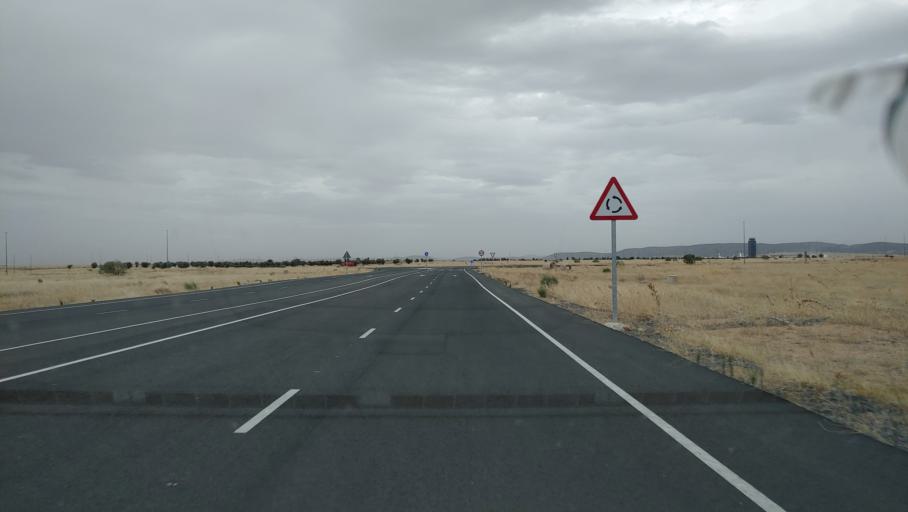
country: ES
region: Castille-La Mancha
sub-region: Provincia de Ciudad Real
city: Villar del Pozo
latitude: 38.8708
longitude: -3.9859
